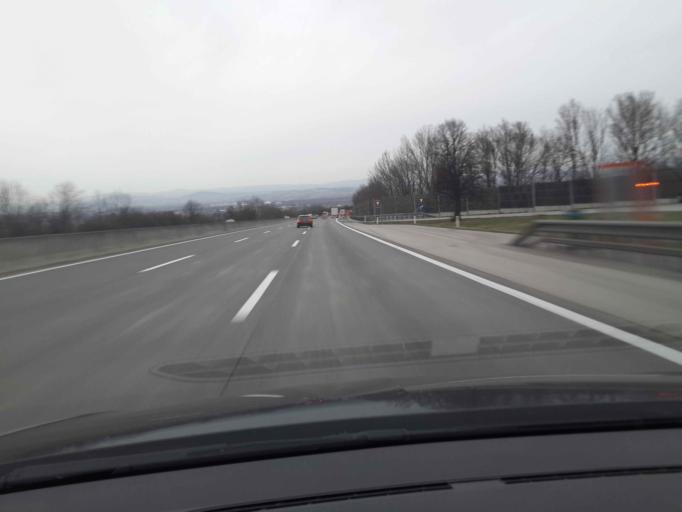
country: AT
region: Lower Austria
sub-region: Politischer Bezirk Amstetten
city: Sankt Valentin
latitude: 48.1643
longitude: 14.5526
